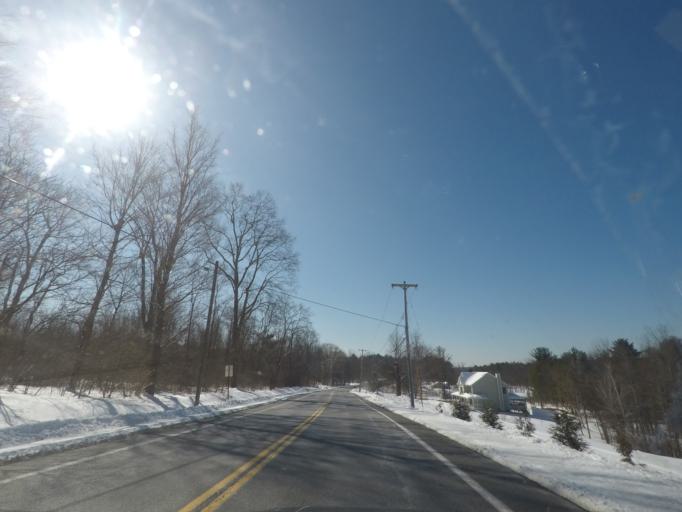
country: US
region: New York
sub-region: Saratoga County
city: Ballston Spa
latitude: 42.9932
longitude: -73.8271
